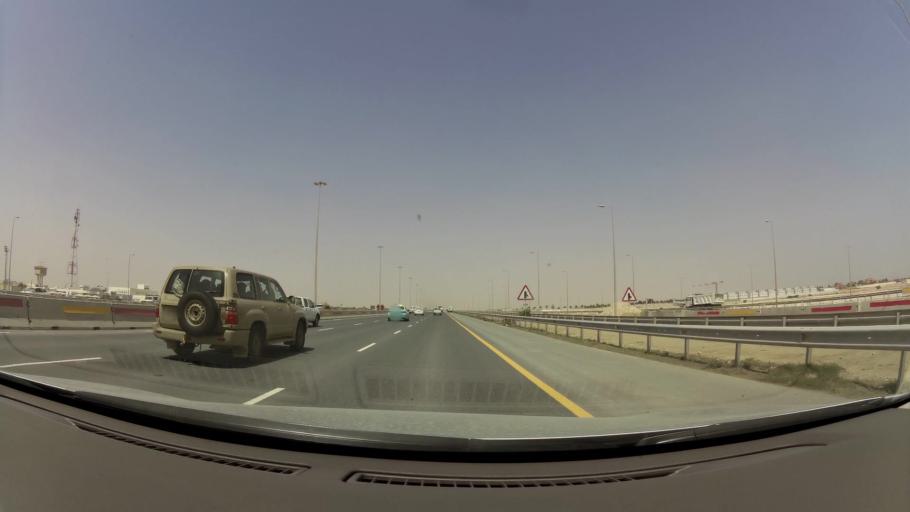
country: QA
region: Baladiyat Umm Salal
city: Umm Salal `Ali
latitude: 25.4516
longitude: 51.4099
